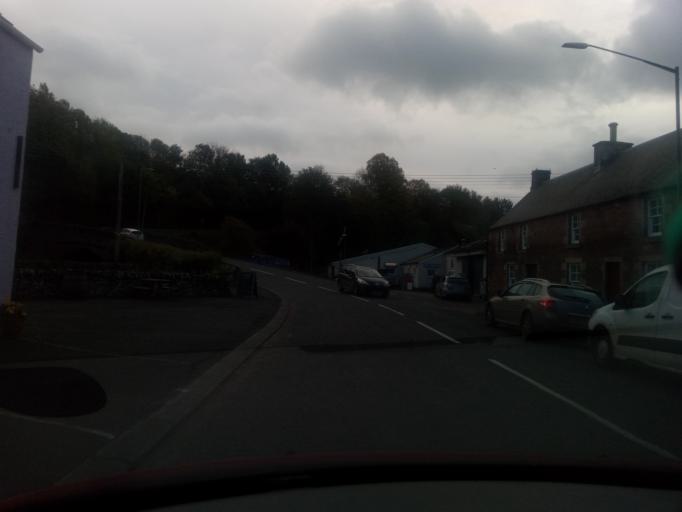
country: GB
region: Scotland
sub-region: The Scottish Borders
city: Jedburgh
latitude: 55.4000
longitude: -2.6554
